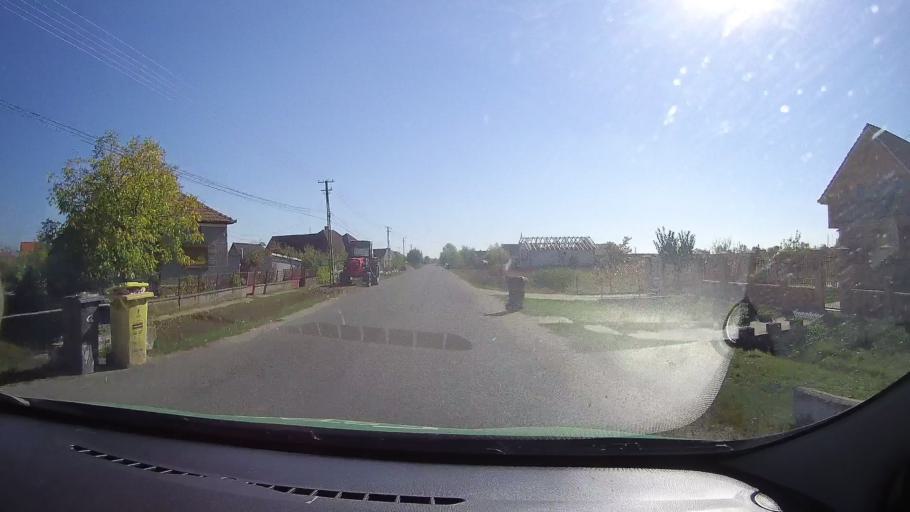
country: RO
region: Satu Mare
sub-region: Comuna Doba
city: Doba
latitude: 47.7421
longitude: 22.7148
